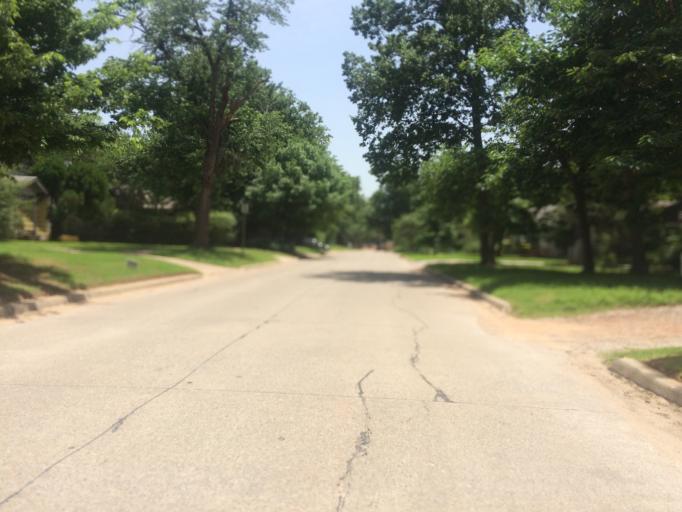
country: US
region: Oklahoma
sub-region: Cleveland County
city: Norman
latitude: 35.2065
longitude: -97.4546
